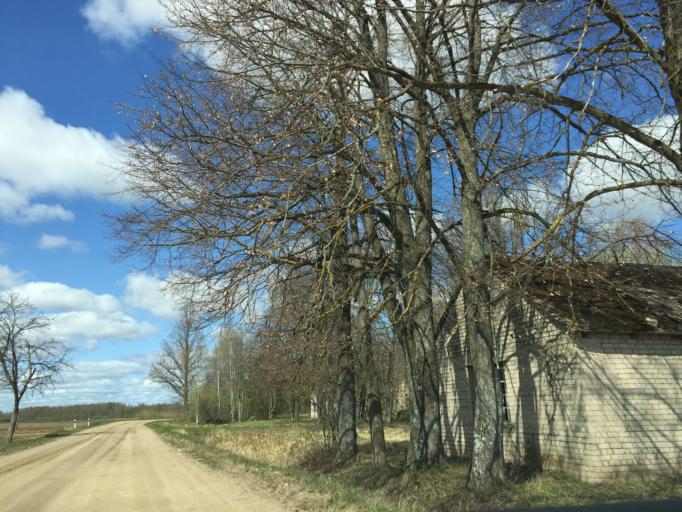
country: LV
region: Vilanu
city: Vilani
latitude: 56.6644
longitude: 27.1064
